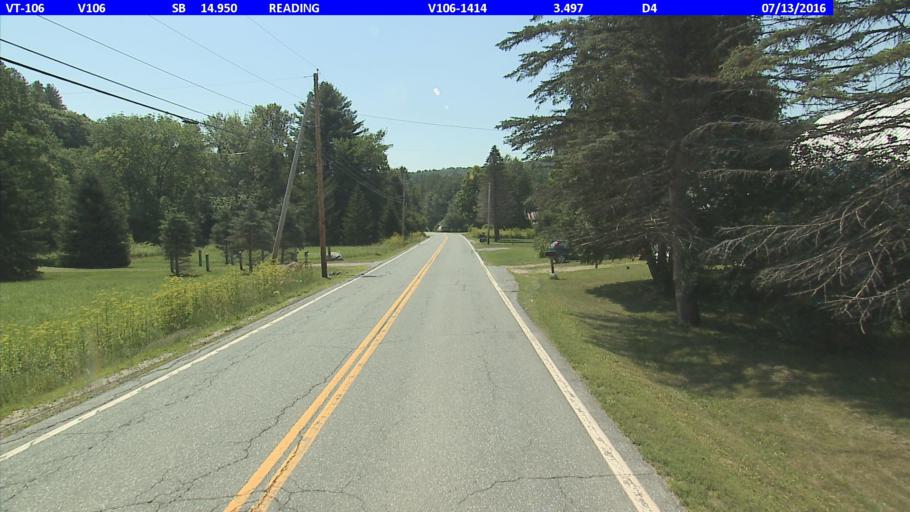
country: US
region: Vermont
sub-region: Windsor County
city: Woodstock
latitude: 43.4878
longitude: -72.5540
